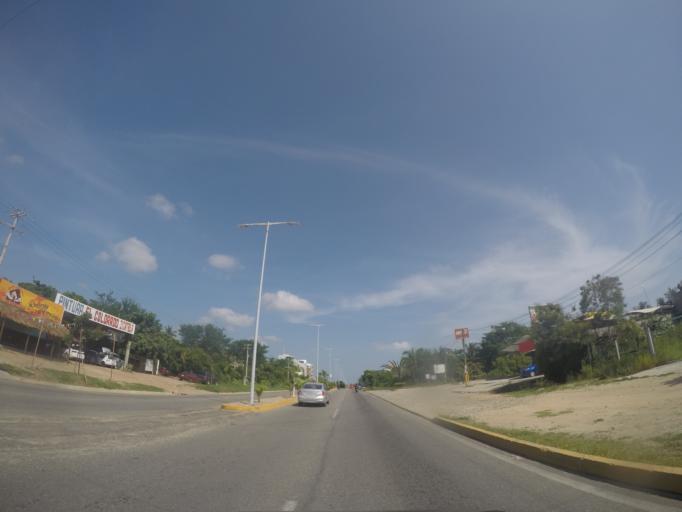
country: MX
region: Oaxaca
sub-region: Santa Maria Colotepec
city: Brisas de Zicatela
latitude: 15.8514
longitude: -97.0516
